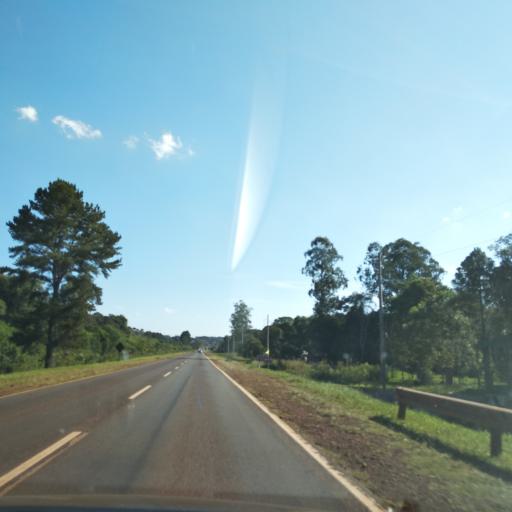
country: AR
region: Misiones
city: Jardin America
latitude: -27.0246
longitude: -55.2074
